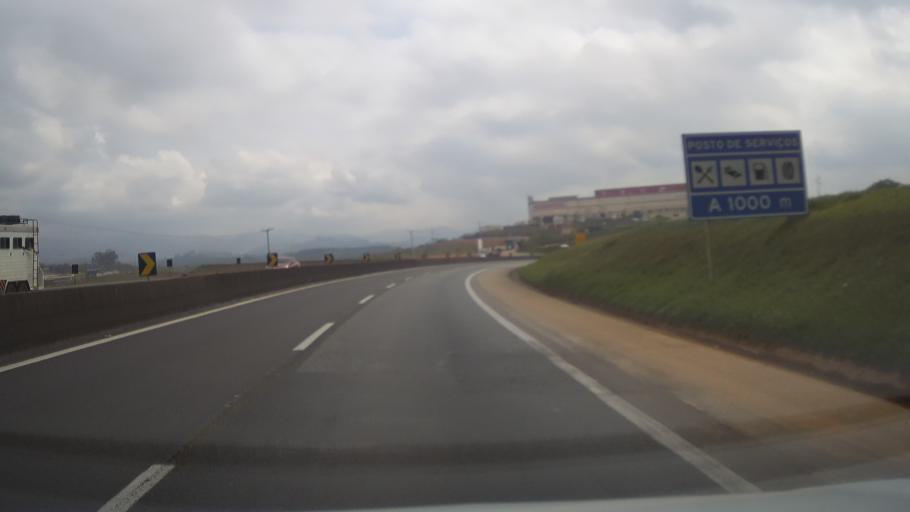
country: BR
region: Minas Gerais
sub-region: Extrema
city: Extrema
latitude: -22.8371
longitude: -46.3271
